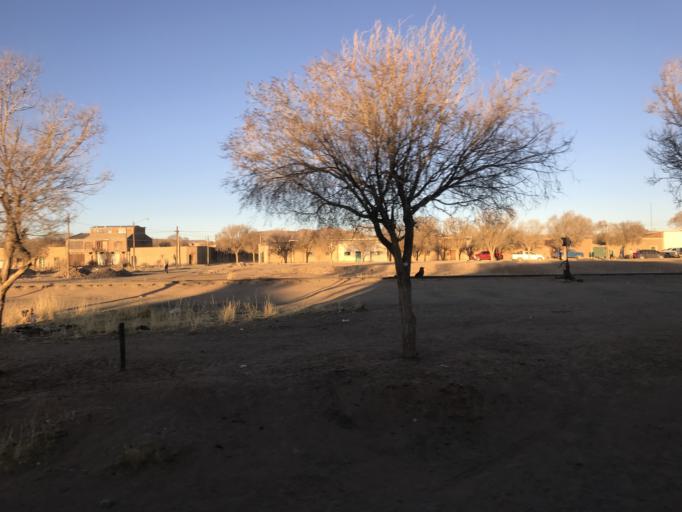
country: AR
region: Jujuy
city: Abra Pampa
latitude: -22.7206
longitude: -65.6960
